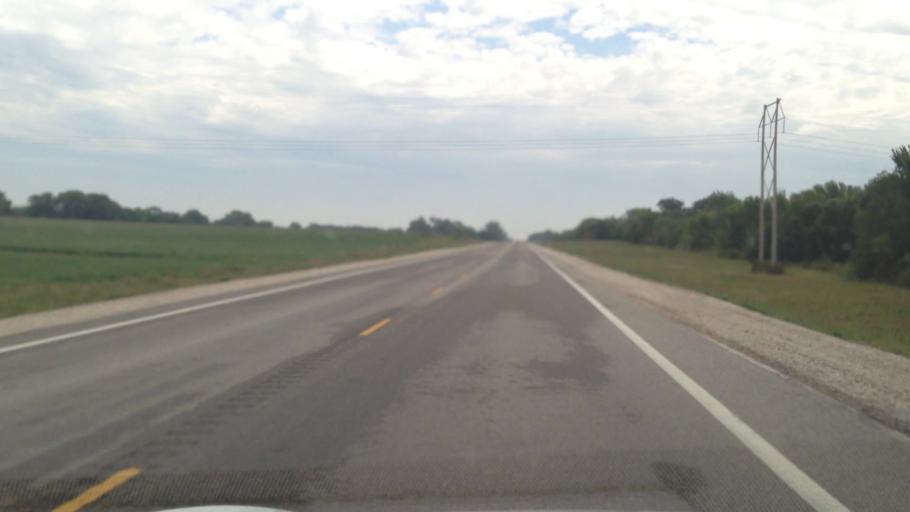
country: US
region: Kansas
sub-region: Allen County
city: Iola
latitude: 37.9109
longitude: -95.1263
